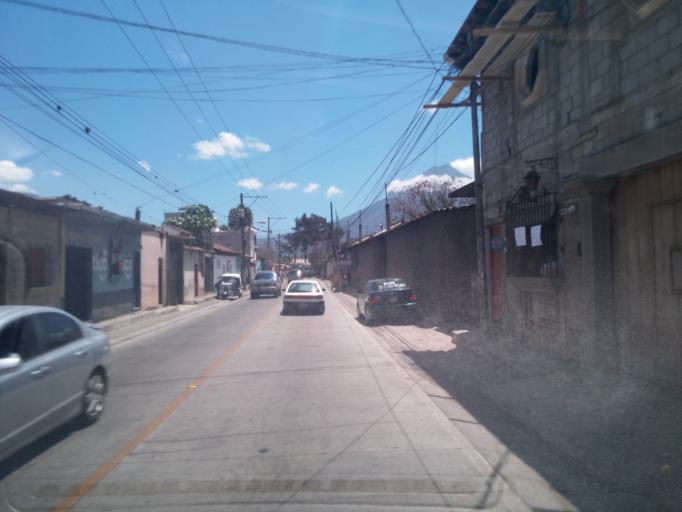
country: GT
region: Sacatepequez
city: Jocotenango
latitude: 14.5820
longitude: -90.7443
